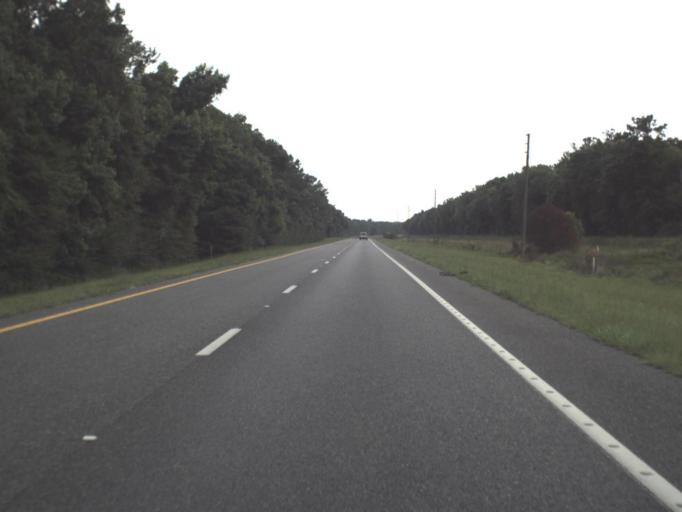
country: US
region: Florida
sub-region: Levy County
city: Inglis
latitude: 29.1805
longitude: -82.6699
